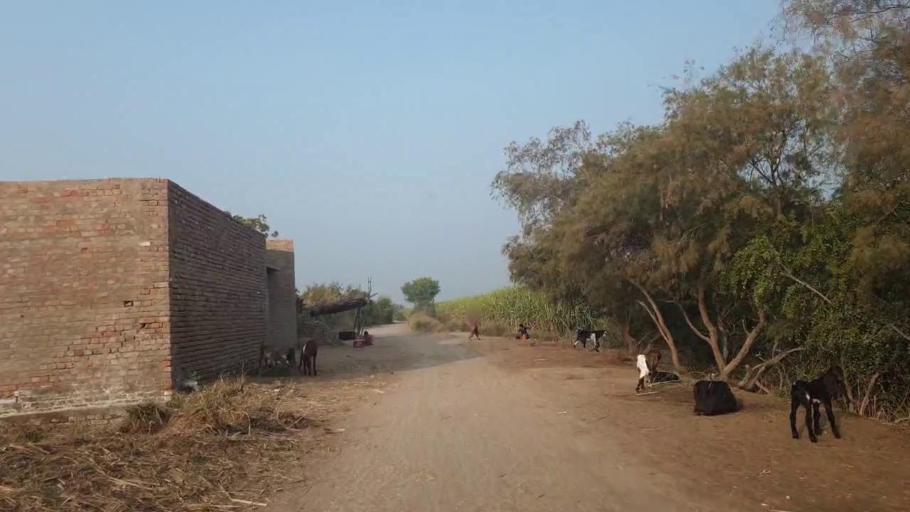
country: PK
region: Sindh
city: Shahdadpur
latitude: 25.8751
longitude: 68.6033
